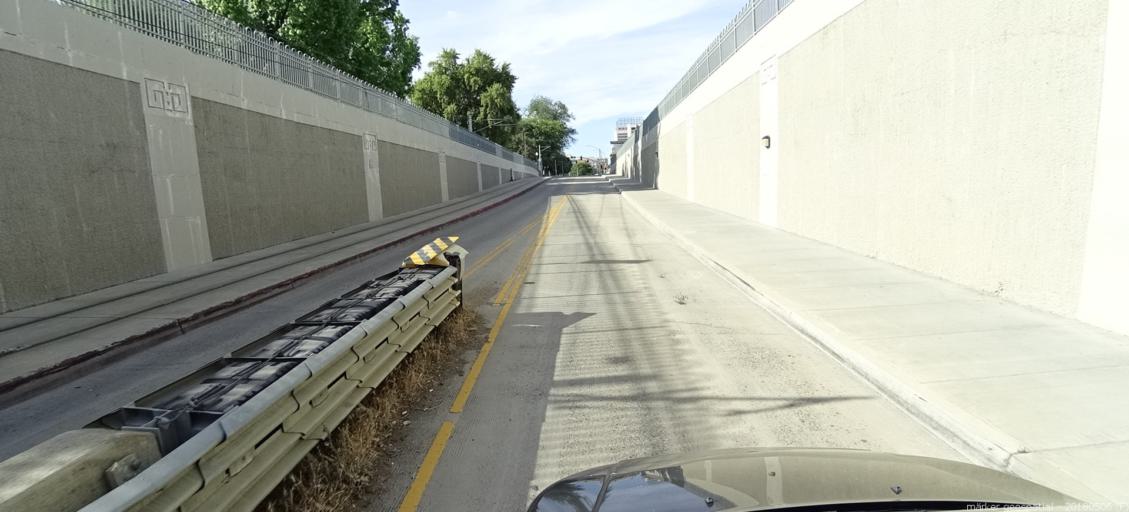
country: US
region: California
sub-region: Sacramento County
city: Sacramento
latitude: 38.5875
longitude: -121.4950
